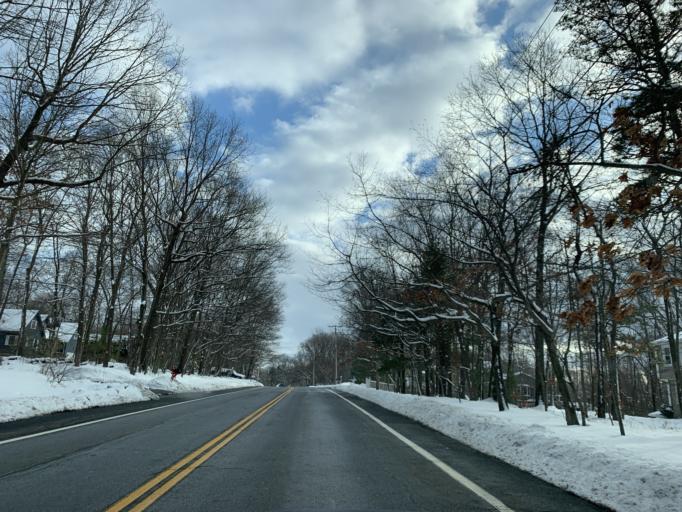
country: US
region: Rhode Island
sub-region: Providence County
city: Cumberland Hill
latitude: 41.9996
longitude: -71.4567
